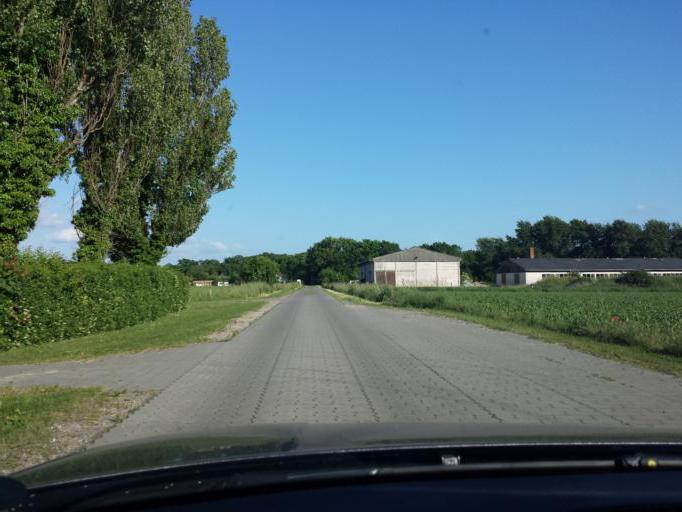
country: DE
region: Brandenburg
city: Ruthnick
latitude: 52.8230
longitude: 12.9530
